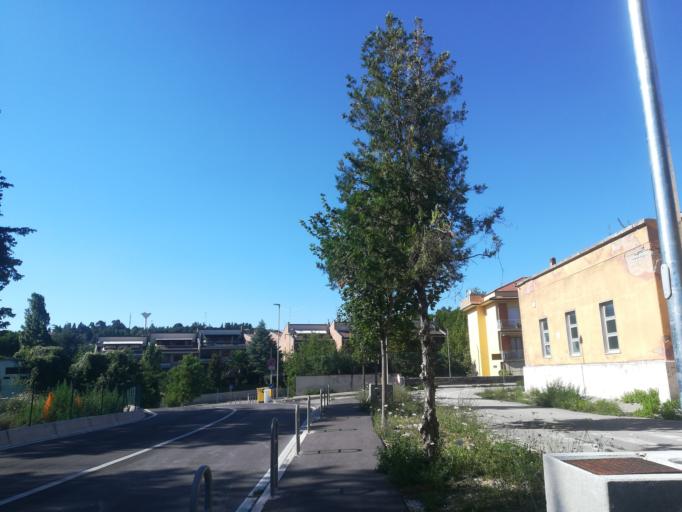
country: IT
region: The Marches
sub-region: Provincia di Macerata
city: Macerata
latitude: 43.2892
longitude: 13.4310
